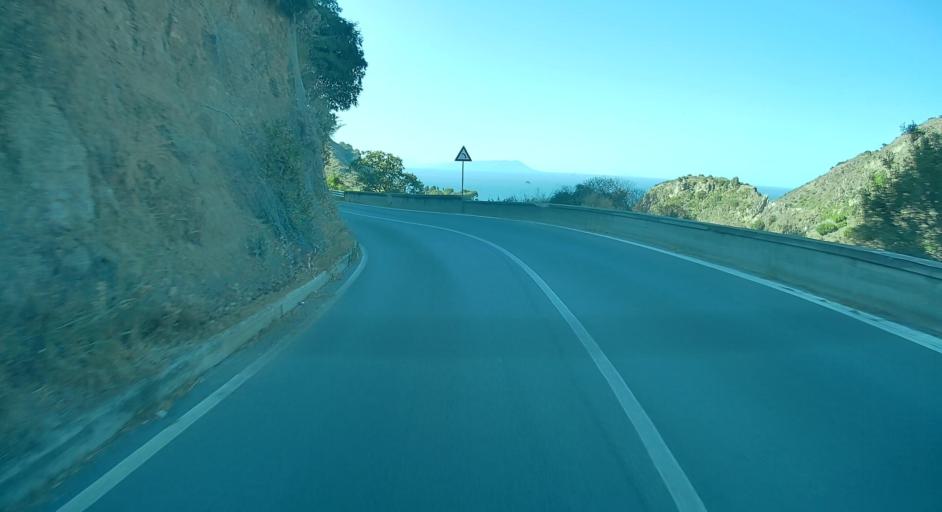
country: IT
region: Sicily
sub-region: Messina
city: Oliveri
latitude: 38.1387
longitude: 15.0333
